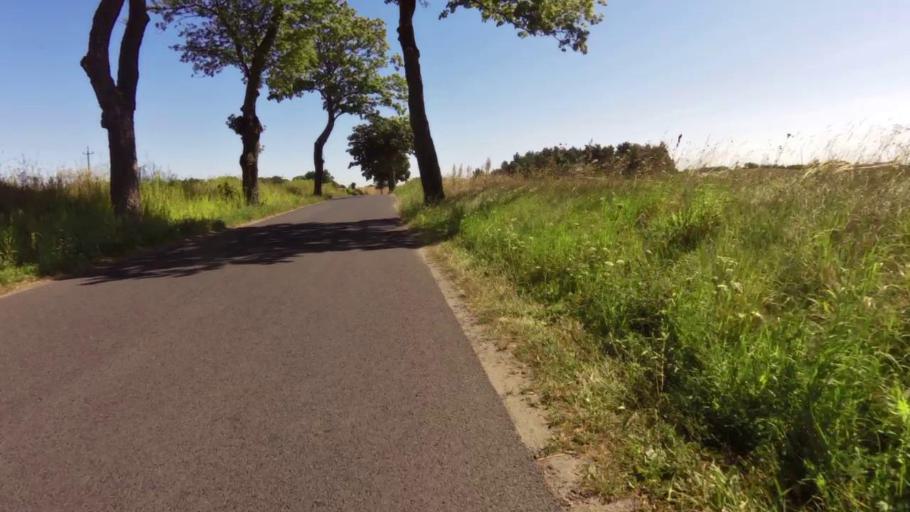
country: PL
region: West Pomeranian Voivodeship
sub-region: Powiat drawski
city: Czaplinek
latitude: 53.5607
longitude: 16.2480
